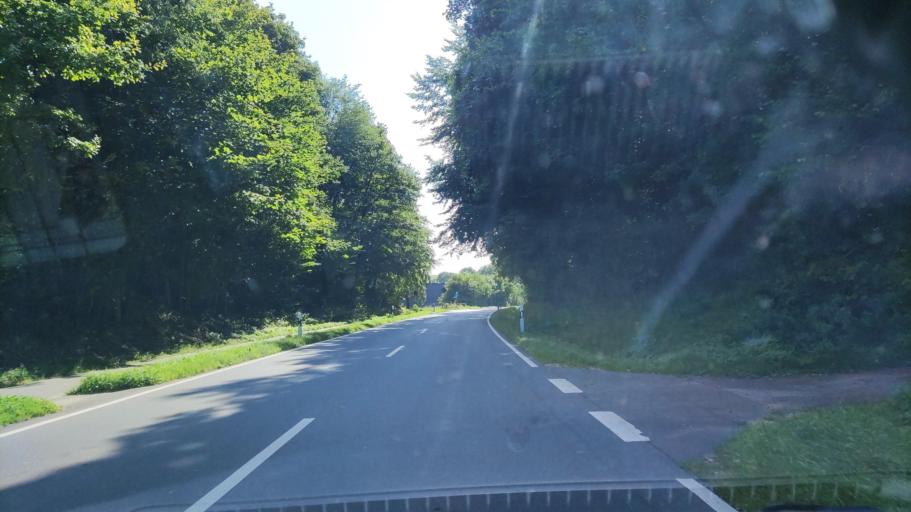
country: DE
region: Schleswig-Holstein
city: Neu Duvenstedt
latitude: 54.3756
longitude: 9.6735
